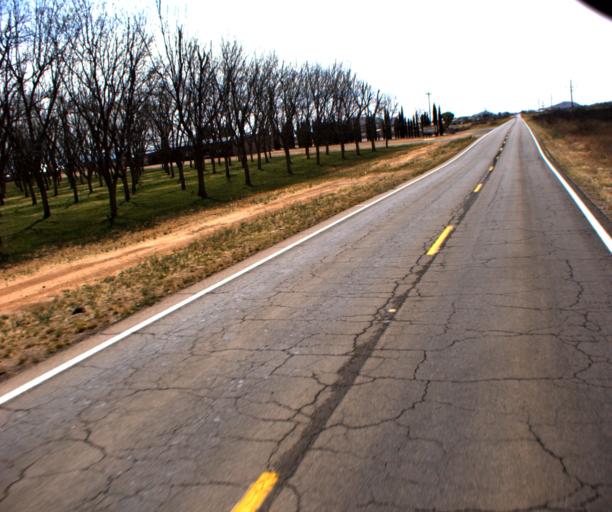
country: US
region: Arizona
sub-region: Cochise County
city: Willcox
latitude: 31.9673
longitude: -109.8446
